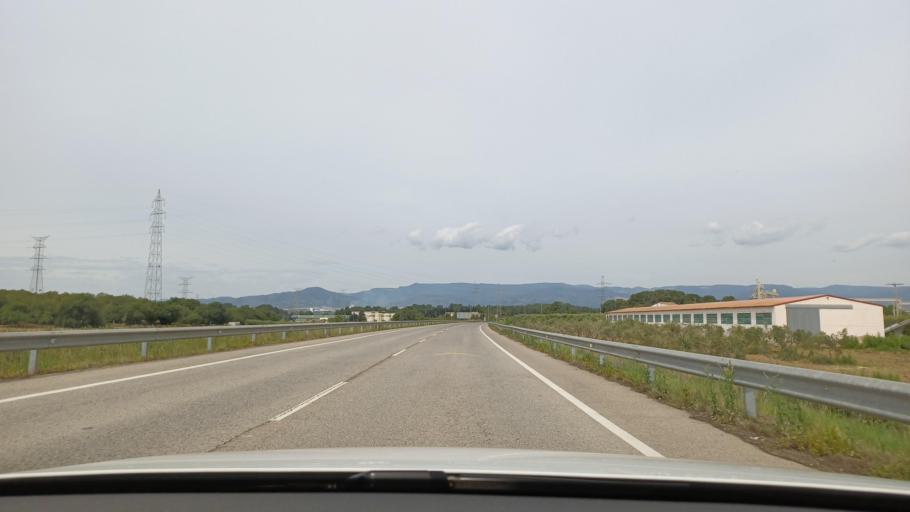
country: ES
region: Catalonia
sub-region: Provincia de Tarragona
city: La Secuita
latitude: 41.1988
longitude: 1.2510
